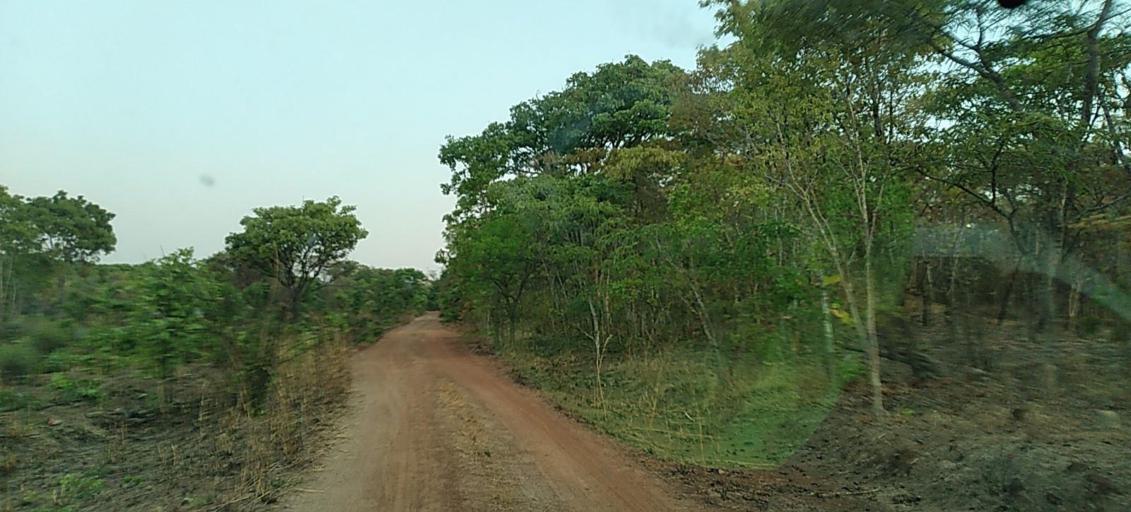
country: ZM
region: North-Western
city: Kalengwa
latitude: -13.1153
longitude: 25.1703
